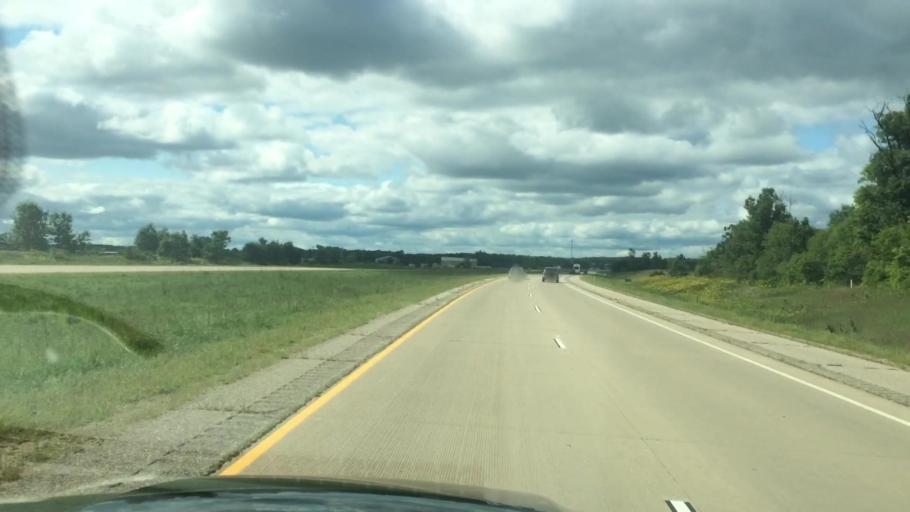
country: US
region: Wisconsin
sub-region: Portage County
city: Amherst
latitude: 44.5030
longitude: -89.4060
